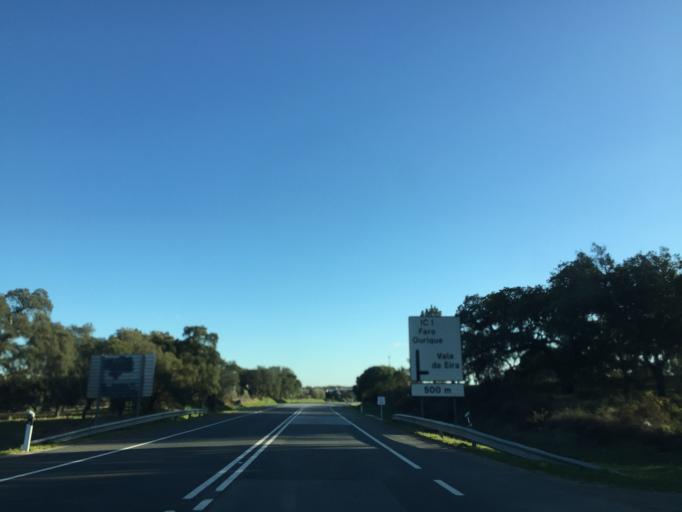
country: PT
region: Setubal
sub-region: Grandola
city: Grandola
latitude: 38.0546
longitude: -8.4034
